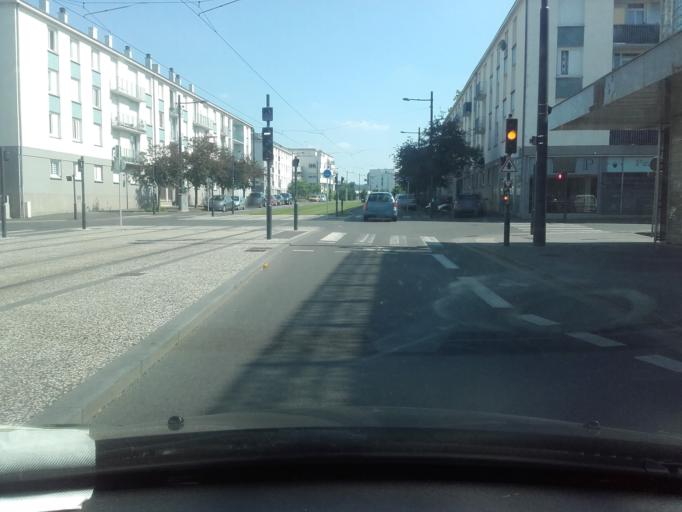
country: FR
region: Centre
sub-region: Departement d'Indre-et-Loire
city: Saint-Cyr-sur-Loire
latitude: 47.4214
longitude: 0.6835
